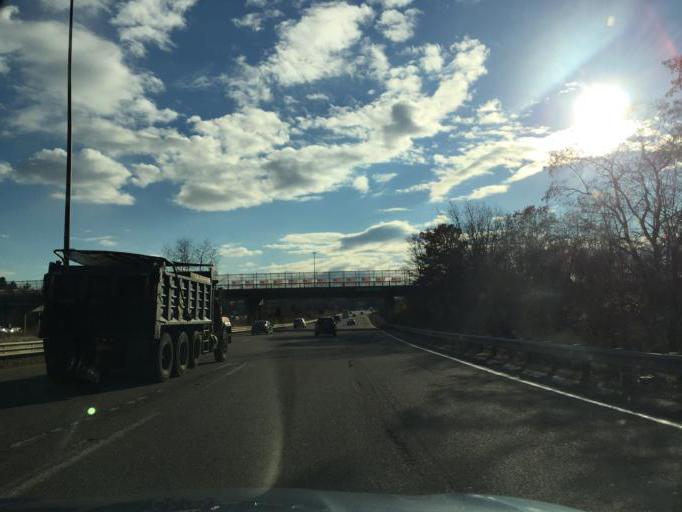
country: US
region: Massachusetts
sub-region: Norfolk County
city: Dedham
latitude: 42.2056
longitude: -71.1417
